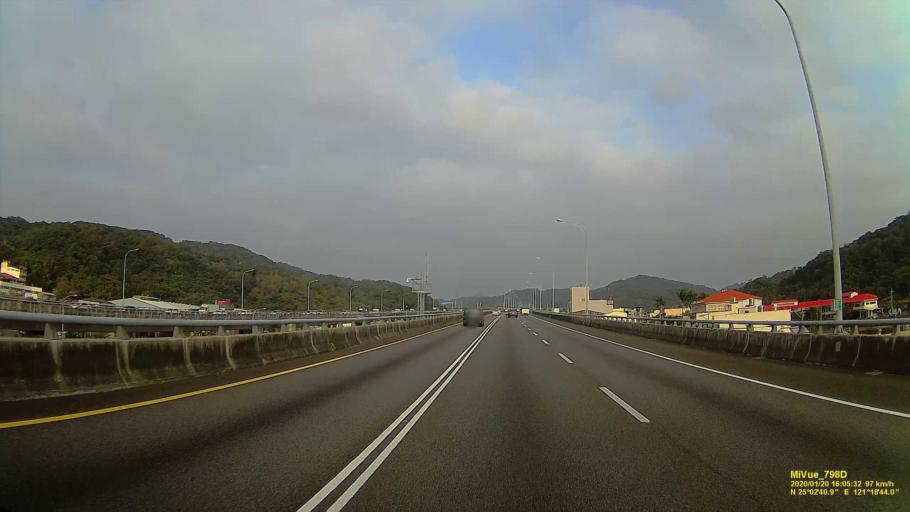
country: TW
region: Taiwan
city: Taoyuan City
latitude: 25.0448
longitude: 121.3131
